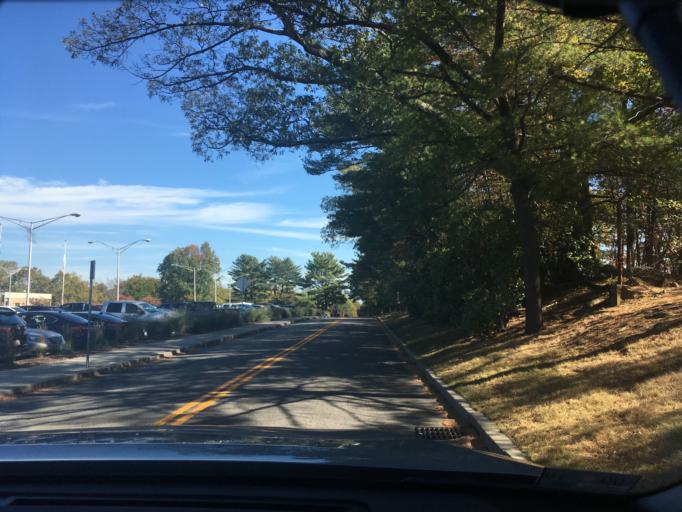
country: US
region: Rhode Island
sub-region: Providence County
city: North Providence
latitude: 41.8412
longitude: -71.4623
